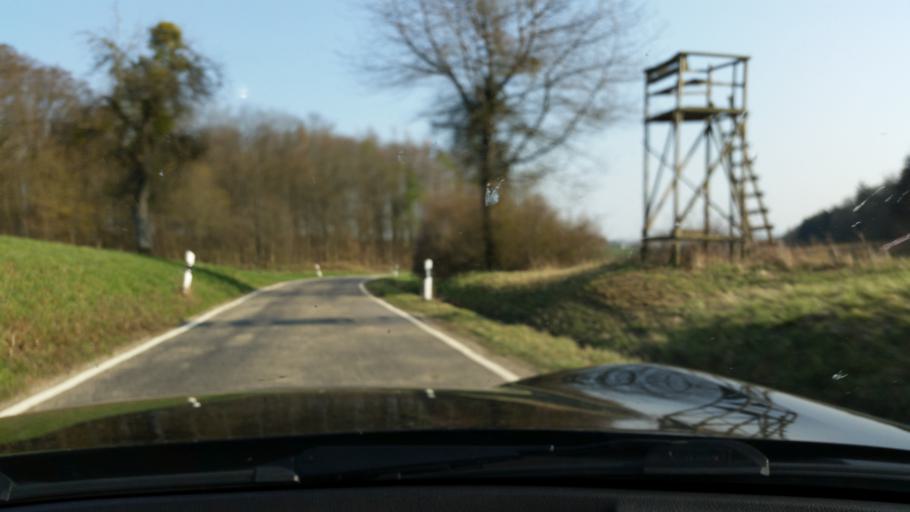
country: DE
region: Baden-Wuerttemberg
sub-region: Regierungsbezirk Stuttgart
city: Jagsthausen
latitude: 49.3363
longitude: 9.4570
